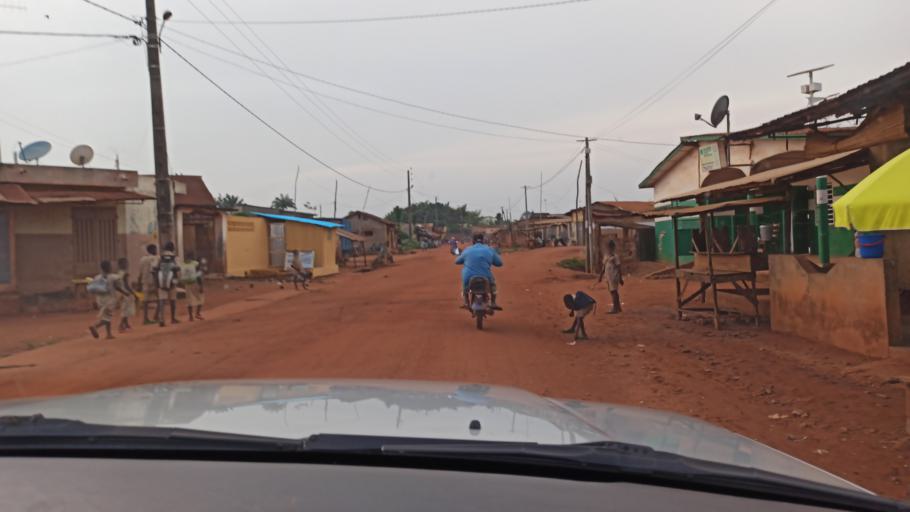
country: BJ
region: Queme
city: Porto-Novo
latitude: 6.5290
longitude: 2.6662
